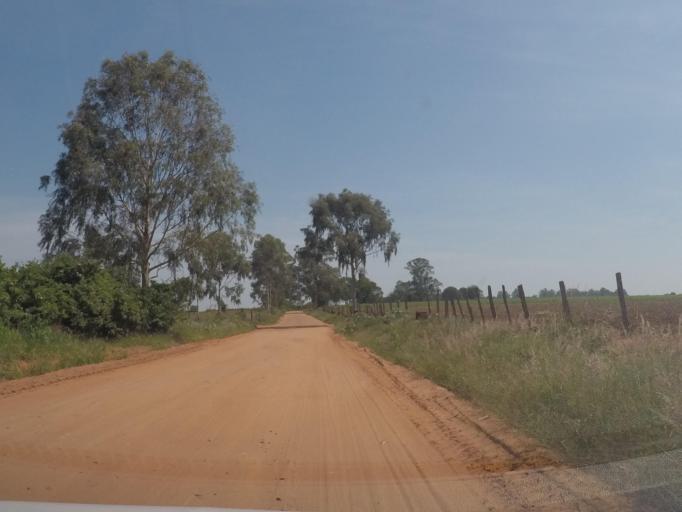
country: BR
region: Sao Paulo
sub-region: Sumare
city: Sumare
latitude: -22.8724
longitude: -47.2869
